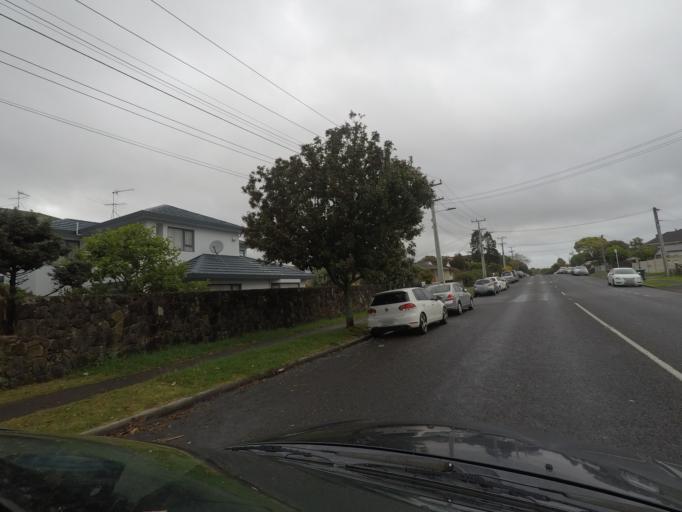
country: NZ
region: Auckland
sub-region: Auckland
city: Auckland
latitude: -36.8847
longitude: 174.7336
